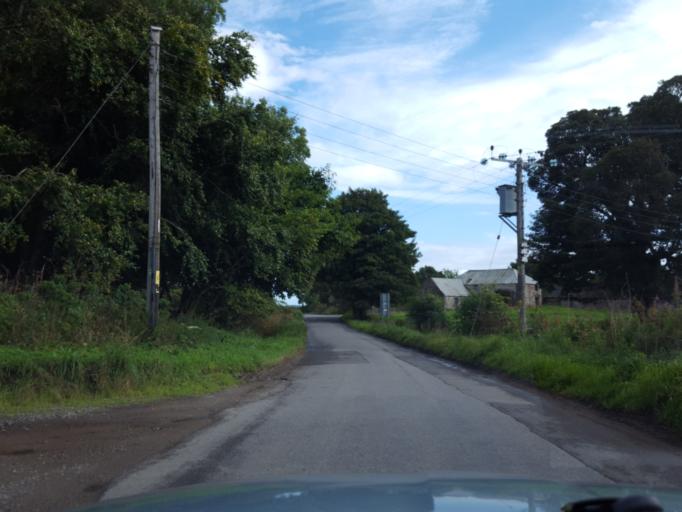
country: GB
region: Scotland
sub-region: Aberdeenshire
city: Laurencekirk
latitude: 56.8686
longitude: -2.5688
